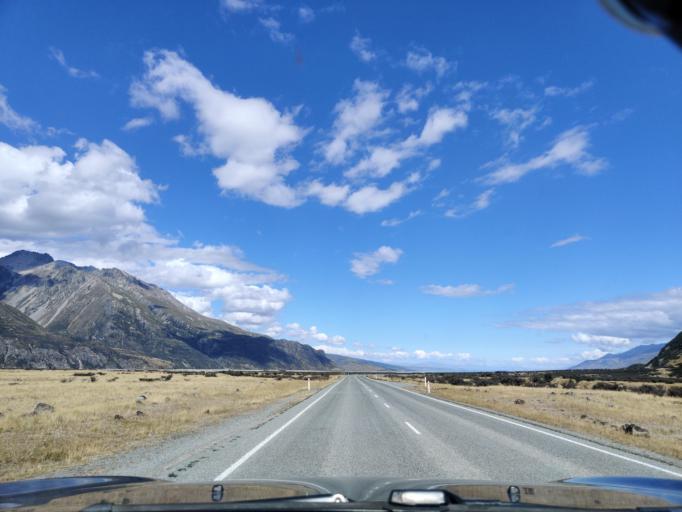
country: NZ
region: Canterbury
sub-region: Timaru District
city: Pleasant Point
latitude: -43.7487
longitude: 170.1167
